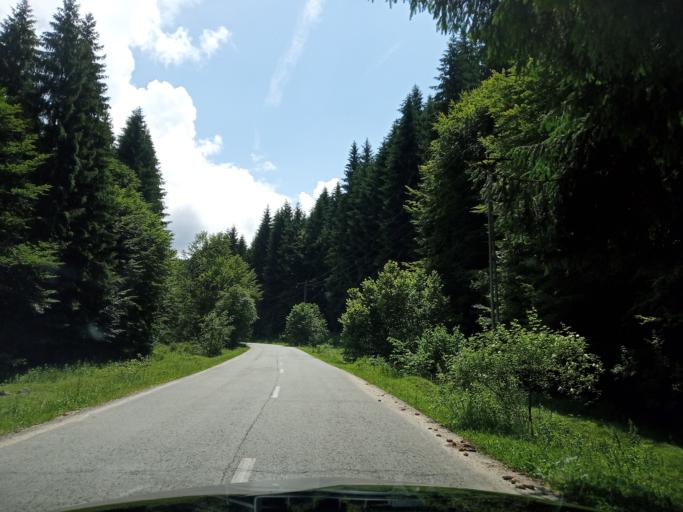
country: RO
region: Hunedoara
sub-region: Oras Petrila
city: Petrila
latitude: 45.3967
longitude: 23.4204
